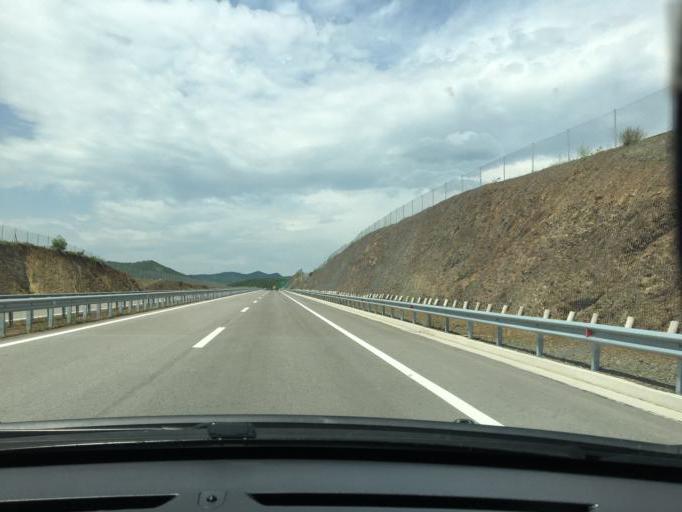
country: MK
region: Gevgelija
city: Miravci
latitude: 41.3131
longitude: 22.4176
